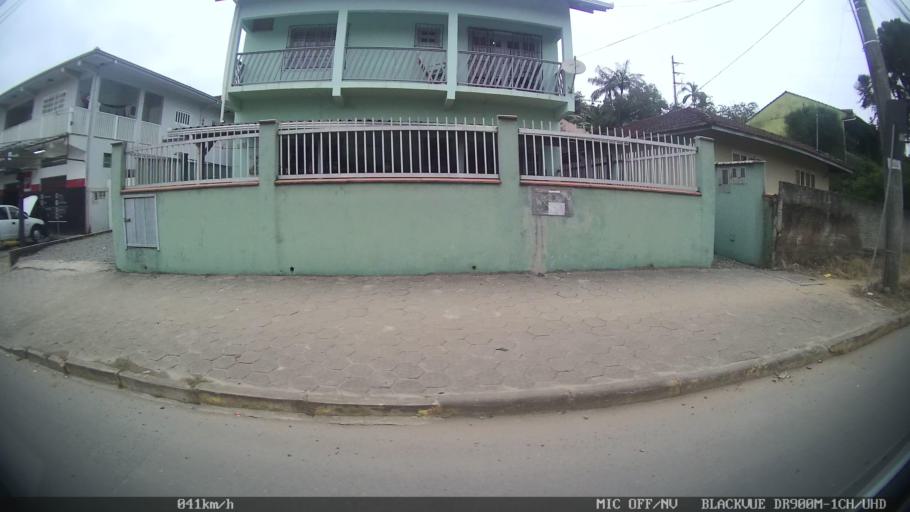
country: BR
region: Santa Catarina
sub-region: Joinville
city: Joinville
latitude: -26.3618
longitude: -48.8187
